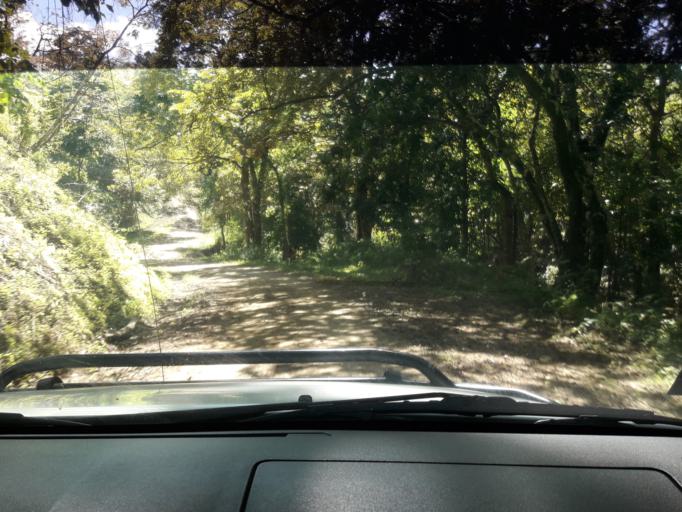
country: CR
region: Guanacaste
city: La Cruz
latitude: 11.2073
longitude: -85.6527
